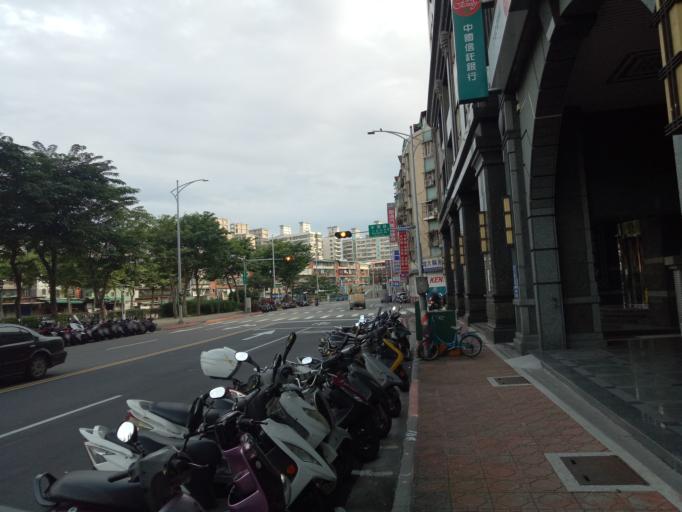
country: TW
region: Taipei
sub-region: Taipei
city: Banqiao
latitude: 25.0470
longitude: 121.4529
